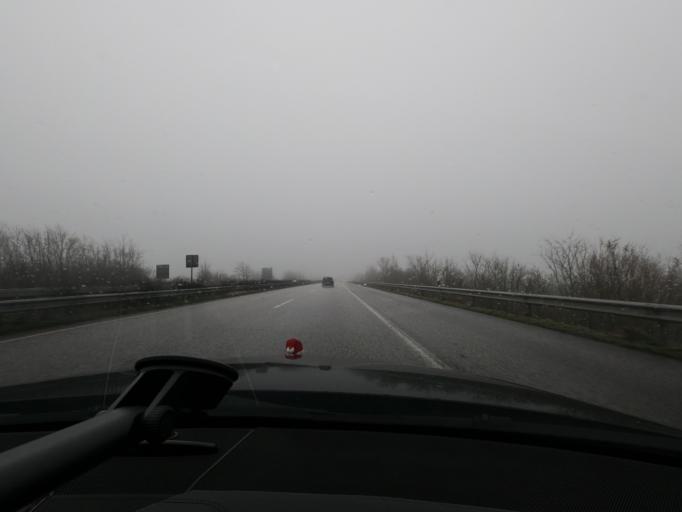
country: DE
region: Schleswig-Holstein
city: Tarp
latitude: 54.6589
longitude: 9.4327
